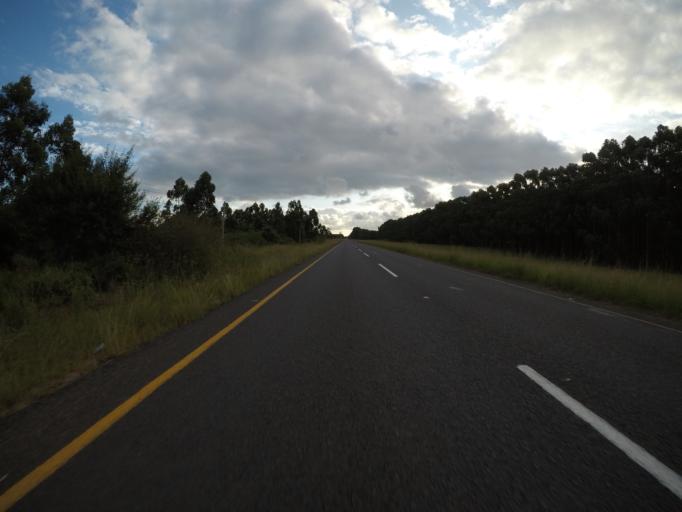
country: ZA
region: KwaZulu-Natal
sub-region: uMkhanyakude District Municipality
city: Mtubatuba
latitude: -28.3939
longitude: 32.2216
